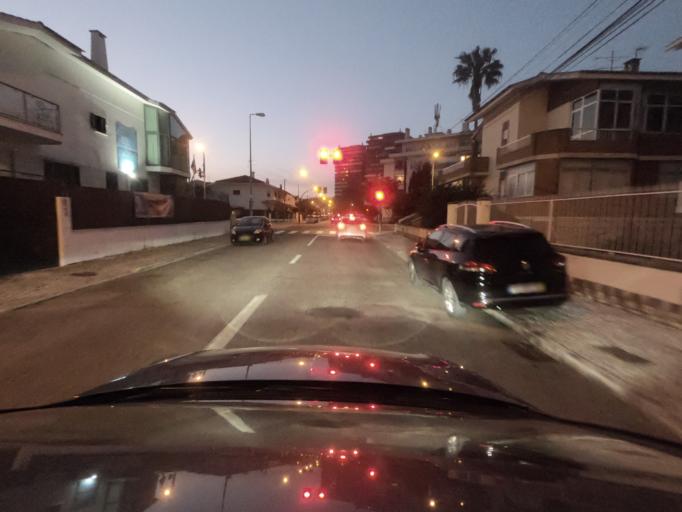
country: PT
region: Lisbon
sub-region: Oeiras
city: Carcavelos
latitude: 38.6900
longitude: -9.3265
